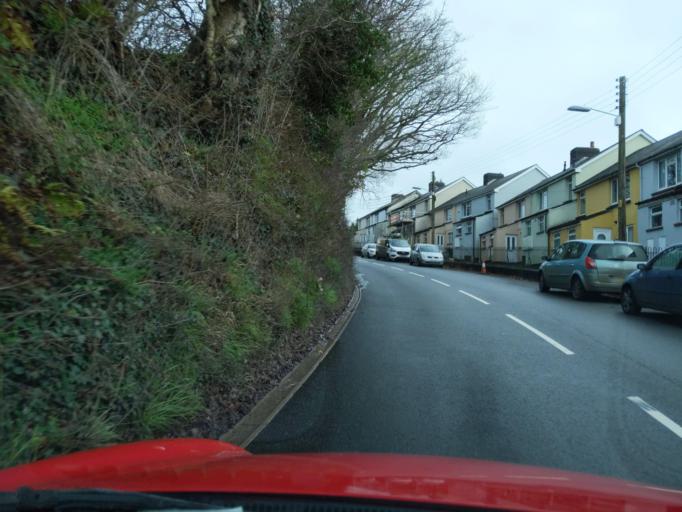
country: GB
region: England
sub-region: Cornwall
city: Launceston
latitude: 50.6441
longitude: -4.3586
